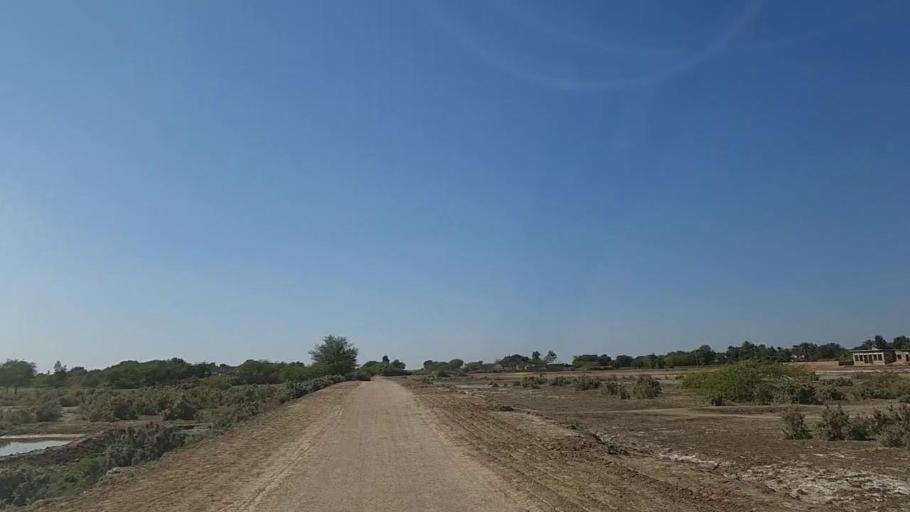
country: PK
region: Sindh
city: Kunri
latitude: 25.2823
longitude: 69.5155
